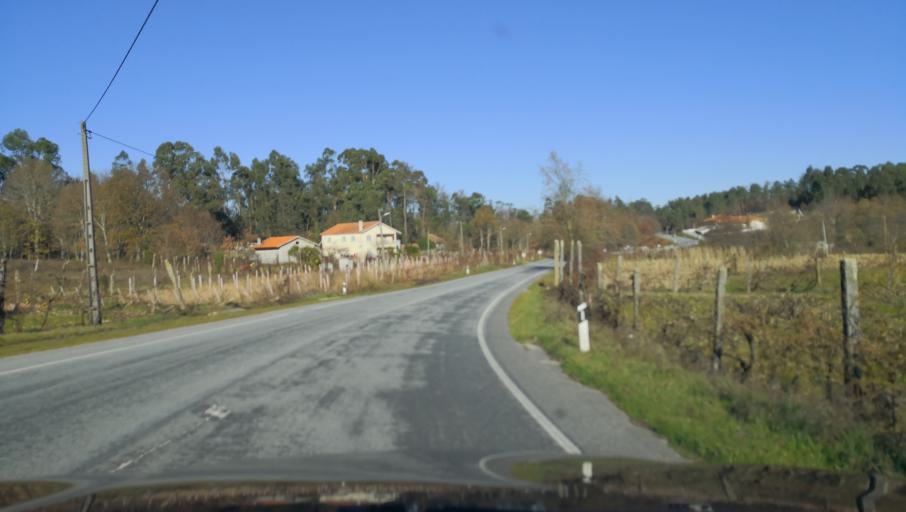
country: PT
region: Viseu
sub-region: Vouzela
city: Vouzela
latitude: 40.7096
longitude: -8.1433
